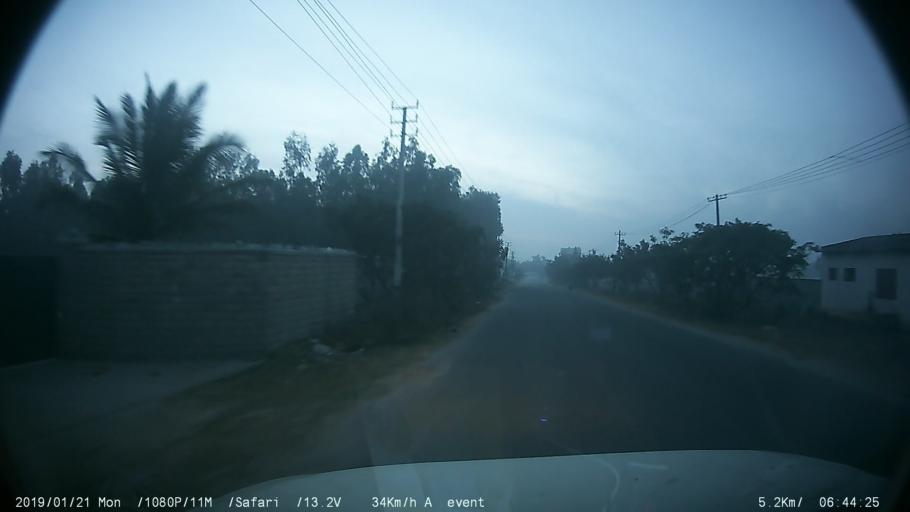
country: IN
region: Karnataka
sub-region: Bangalore Urban
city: Anekal
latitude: 12.8193
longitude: 77.6261
